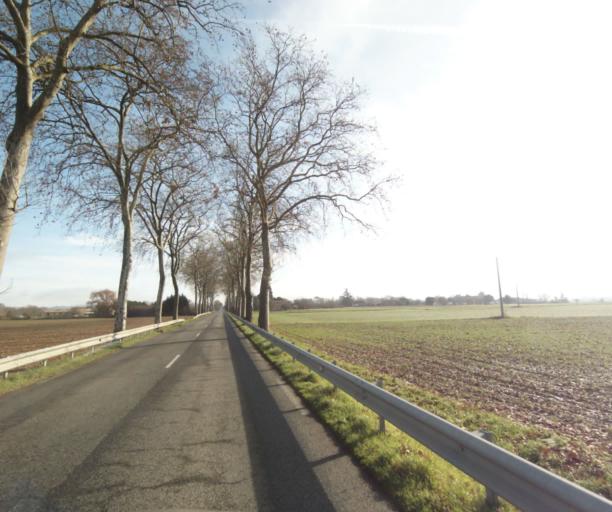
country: FR
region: Midi-Pyrenees
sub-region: Departement du Tarn-et-Garonne
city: Nohic
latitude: 43.8721
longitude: 1.4635
